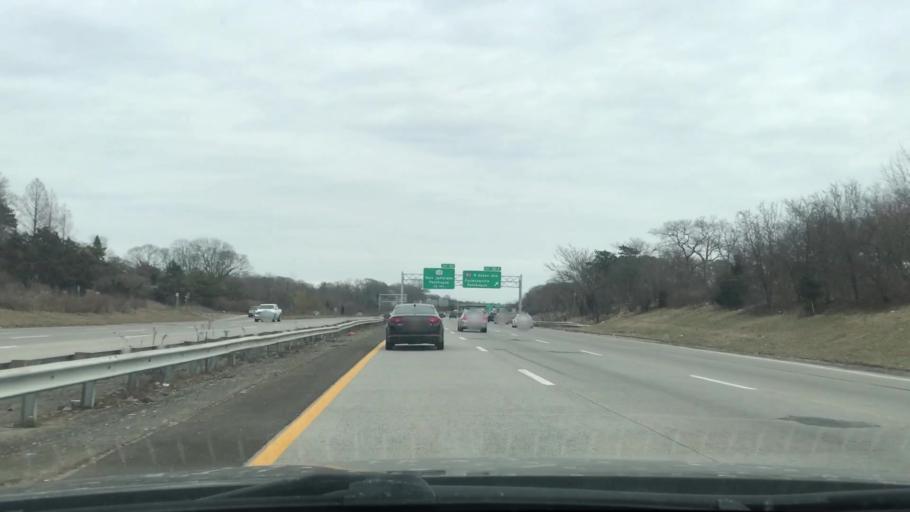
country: US
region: New York
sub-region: Suffolk County
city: Patchogue
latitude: 40.7779
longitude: -73.0268
